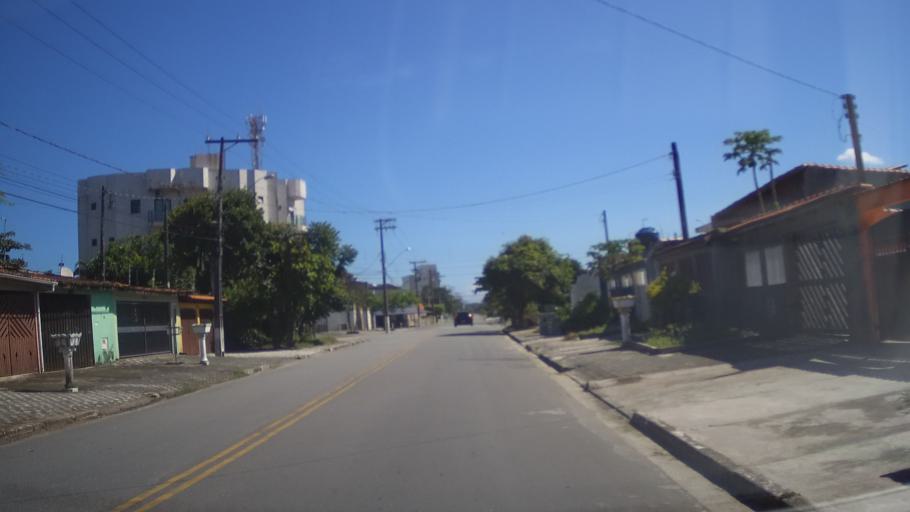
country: BR
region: Sao Paulo
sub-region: Mongagua
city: Mongagua
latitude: -24.1289
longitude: -46.6866
